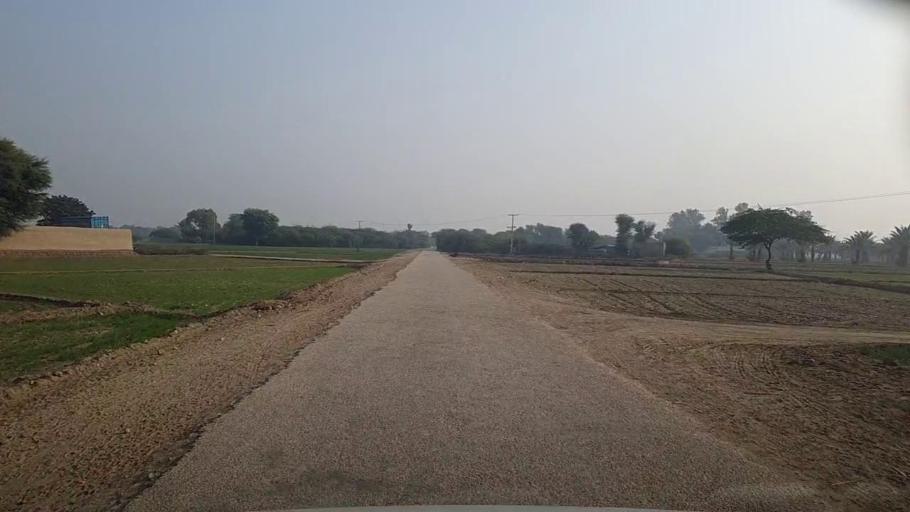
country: PK
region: Sindh
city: Kandiari
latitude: 27.0405
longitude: 68.4781
